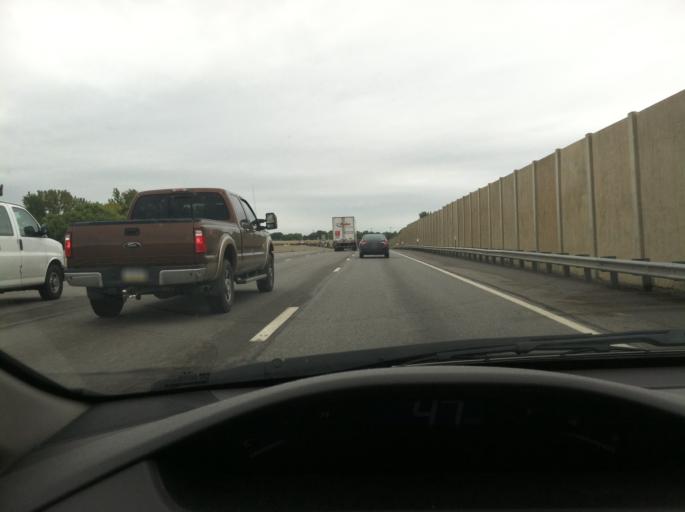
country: US
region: New York
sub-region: Erie County
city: Blasdell
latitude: 42.8012
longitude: -78.8148
